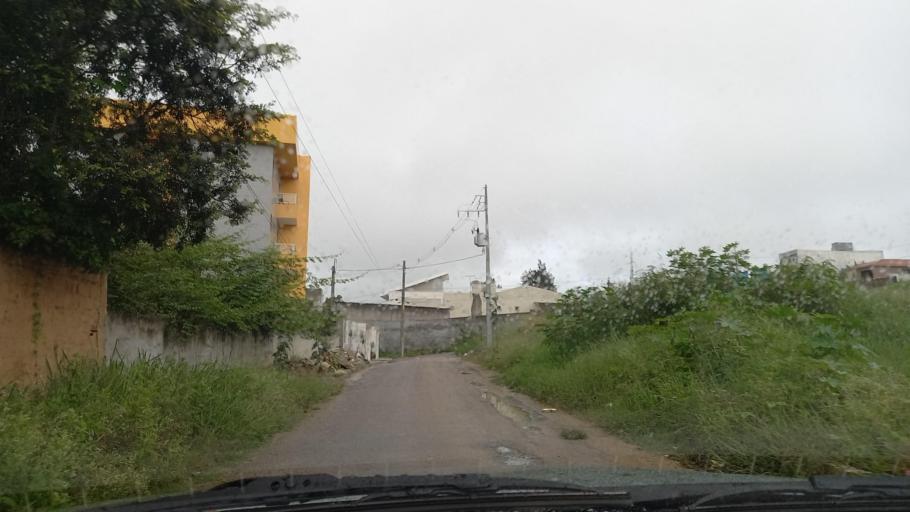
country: BR
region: Pernambuco
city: Garanhuns
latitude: -8.8865
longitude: -36.4967
